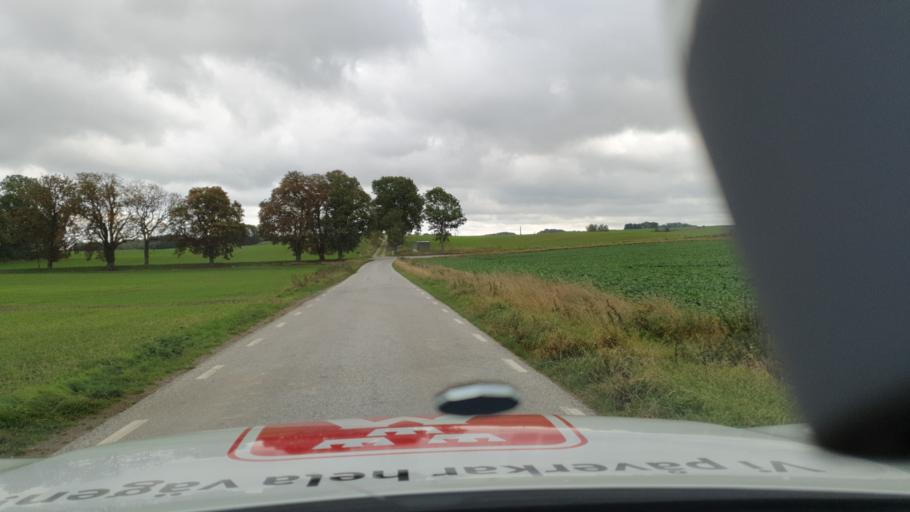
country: SE
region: Skane
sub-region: Svedala Kommun
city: Svedala
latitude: 55.4876
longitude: 13.1880
